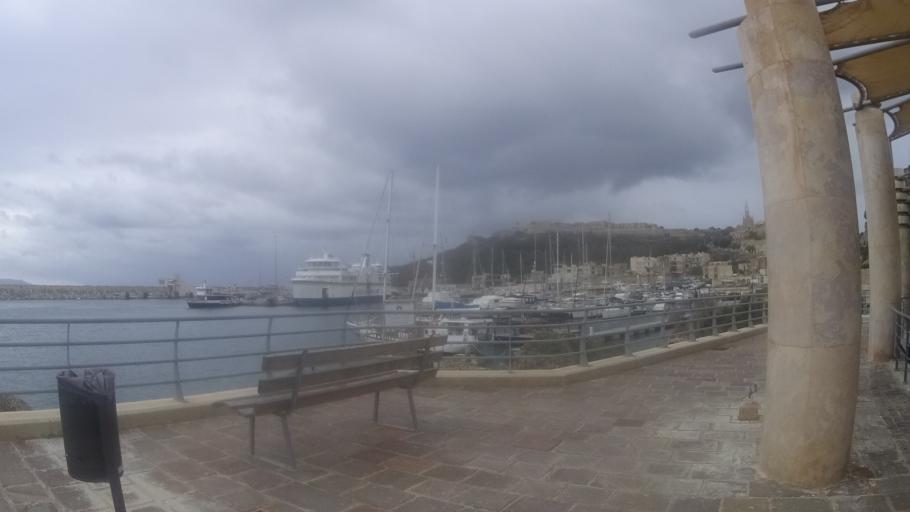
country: MT
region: Ghajnsielem
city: Mgarr
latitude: 36.0268
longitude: 14.2996
